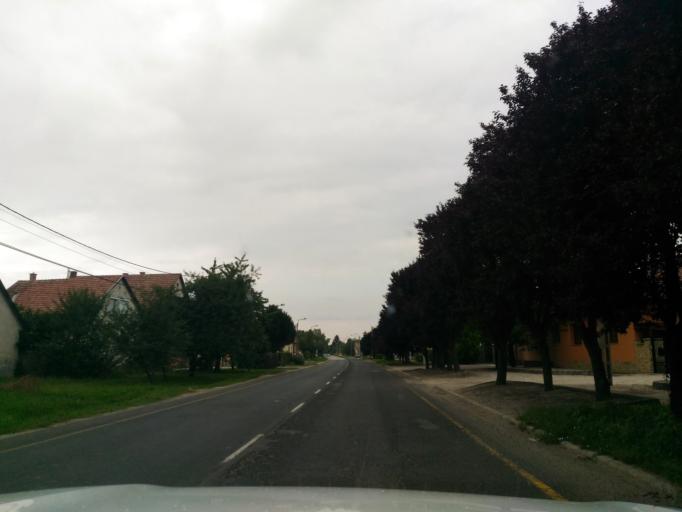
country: HU
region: Pest
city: Alsonemedi
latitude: 47.3077
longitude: 19.1759
